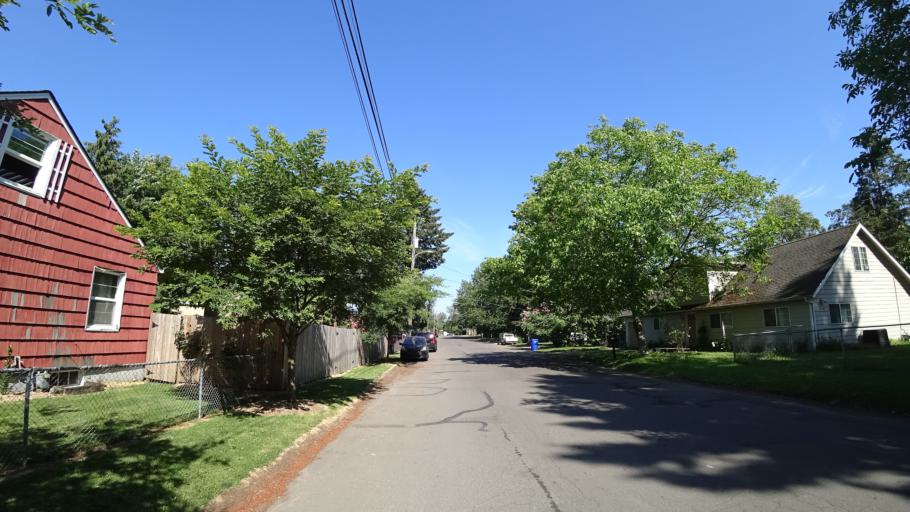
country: US
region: Oregon
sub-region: Multnomah County
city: Lents
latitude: 45.5611
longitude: -122.5711
